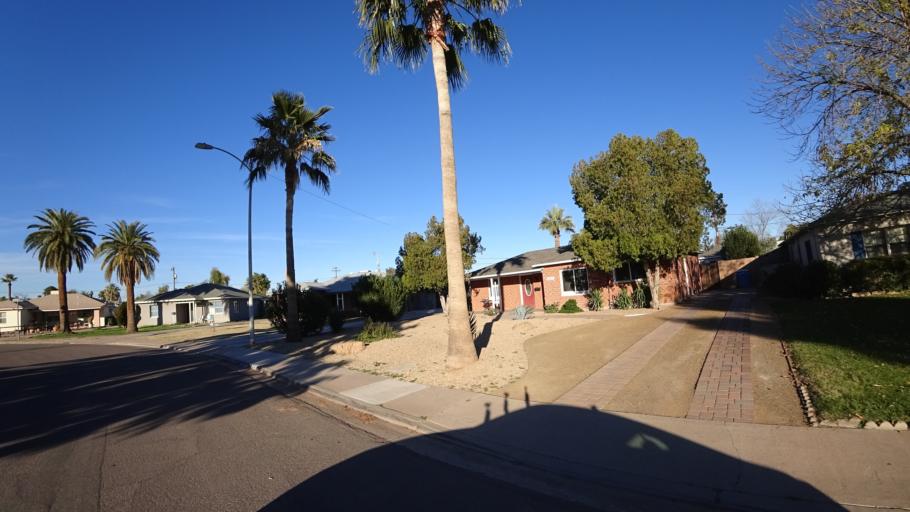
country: US
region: Arizona
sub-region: Maricopa County
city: Phoenix
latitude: 33.4829
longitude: -112.0968
